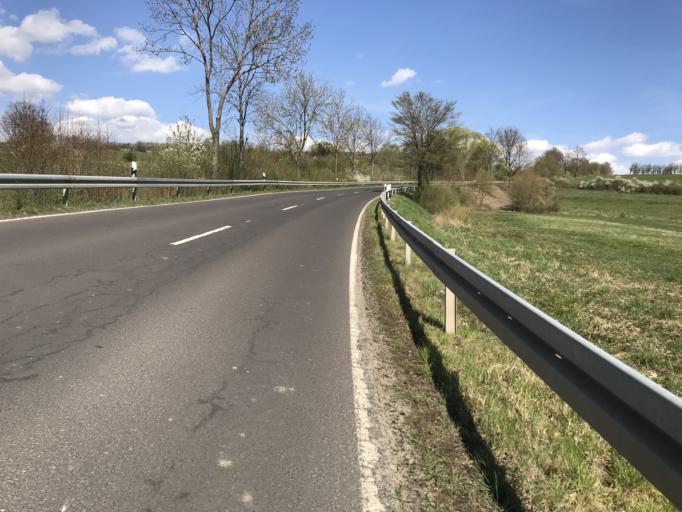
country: DE
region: Hesse
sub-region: Regierungsbezirk Giessen
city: Rabenau
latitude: 50.6845
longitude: 8.8295
